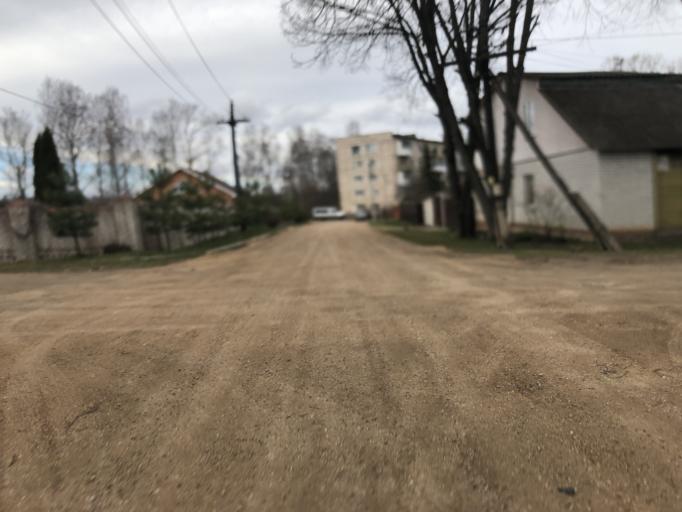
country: RU
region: Tverskaya
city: Rzhev
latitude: 56.2553
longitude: 34.3177
